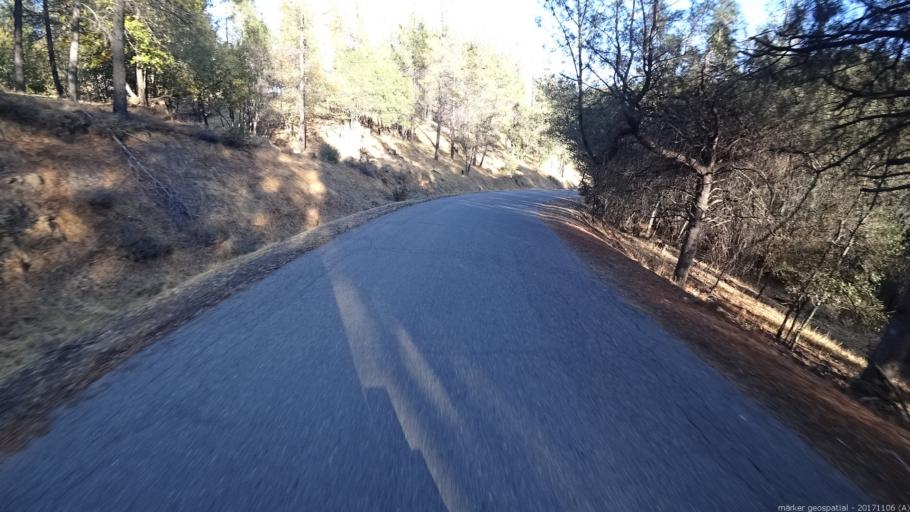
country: US
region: California
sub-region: Shasta County
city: Shasta
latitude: 40.5804
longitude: -122.4902
